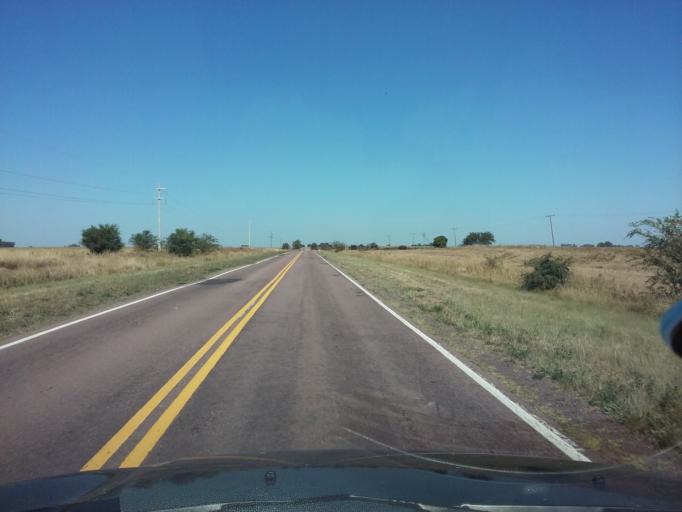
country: AR
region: La Pampa
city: Uriburu
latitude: -36.3839
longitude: -63.9432
